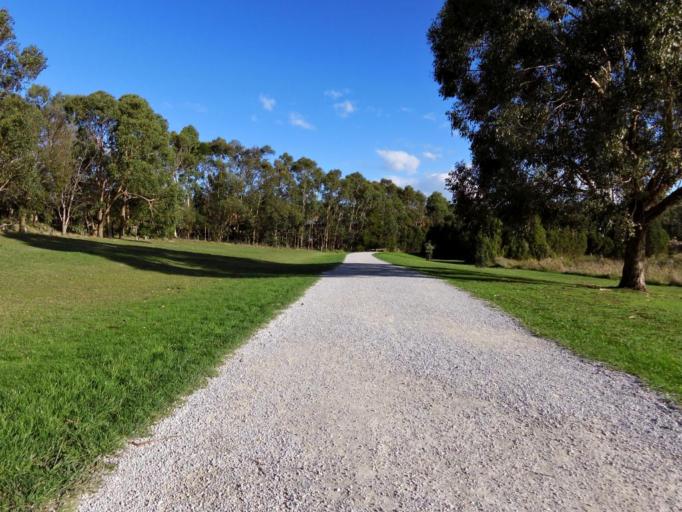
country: AU
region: Victoria
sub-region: Yarra Ranges
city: Lilydale
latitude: -37.7691
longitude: 145.3542
